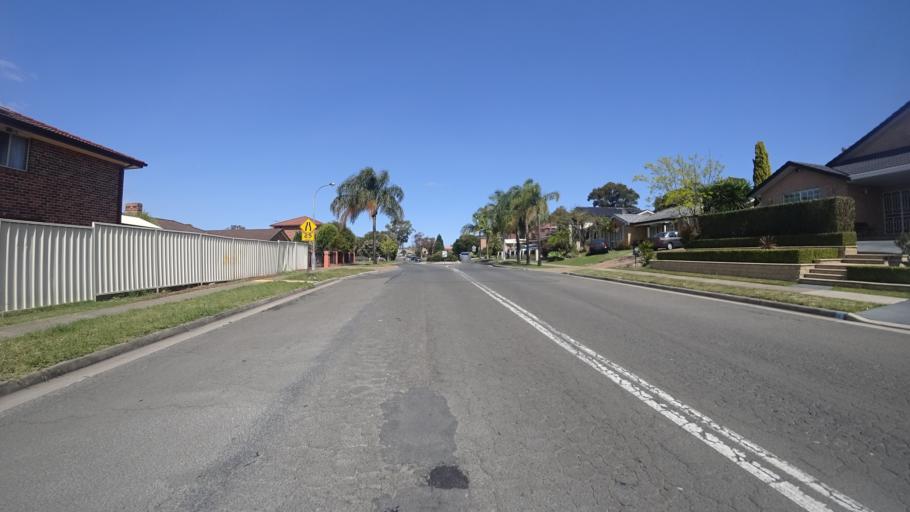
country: AU
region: New South Wales
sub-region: Campbelltown Municipality
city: Glenfield
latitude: -33.9506
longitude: 150.8957
